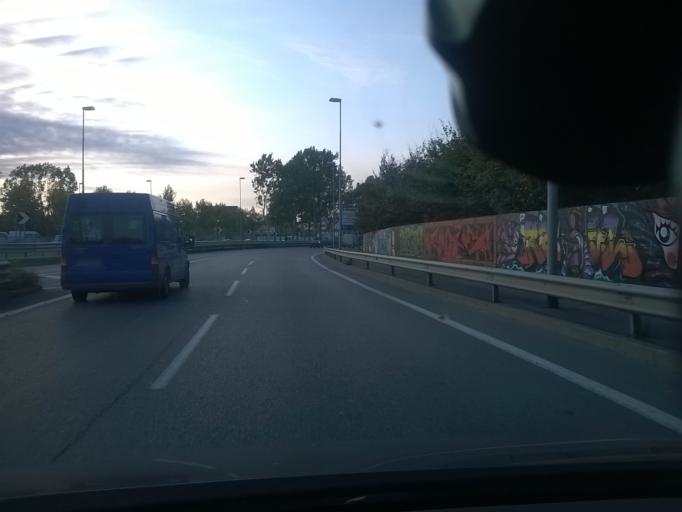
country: IT
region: Lombardy
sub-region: Provincia di Bergamo
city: Gorle
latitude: 45.7020
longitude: 9.6952
